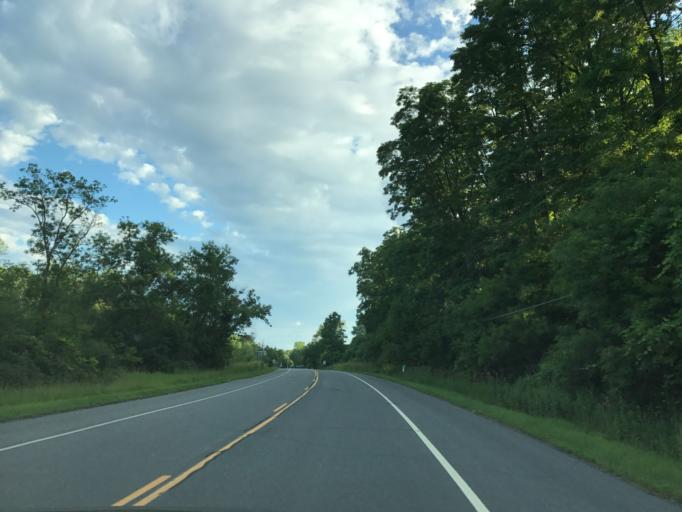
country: US
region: New York
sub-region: Saratoga County
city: Stillwater
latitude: 42.9763
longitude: -73.6305
